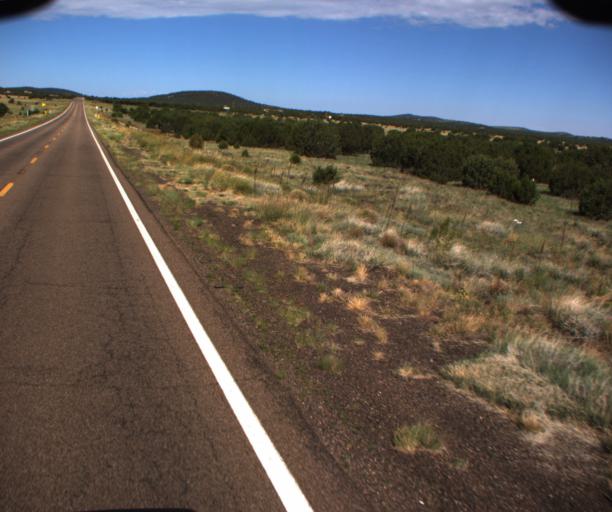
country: US
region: Arizona
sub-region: Navajo County
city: Pinetop-Lakeside
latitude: 34.2720
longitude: -109.6968
